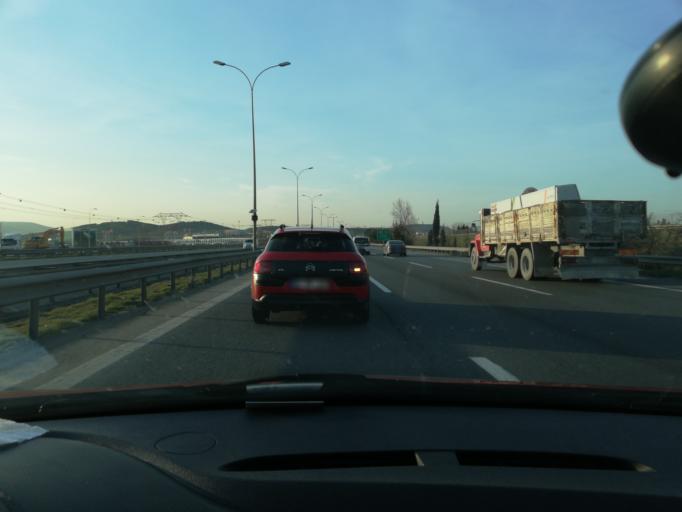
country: TR
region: Kocaeli
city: Balcik
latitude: 40.9095
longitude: 29.3589
